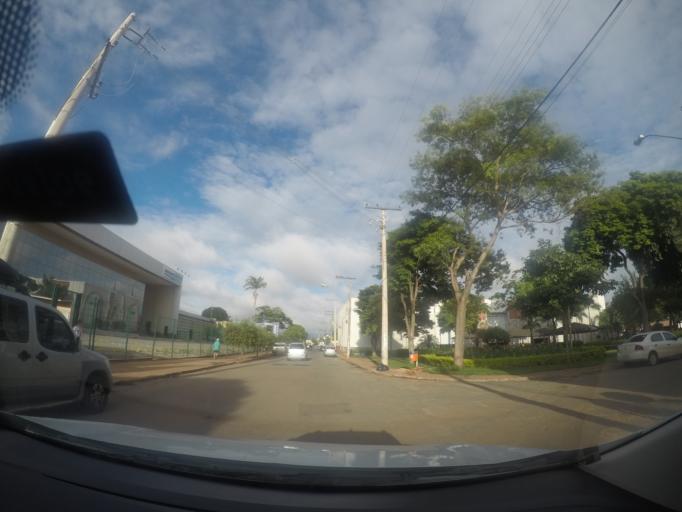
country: BR
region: Goias
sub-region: Goiania
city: Goiania
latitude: -16.6902
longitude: -49.3116
